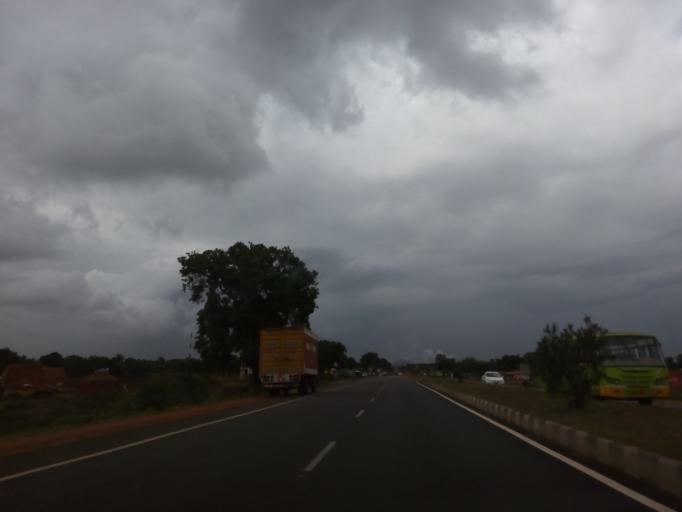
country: IN
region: Karnataka
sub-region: Davanagere
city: Harihar
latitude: 14.5382
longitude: 75.7602
